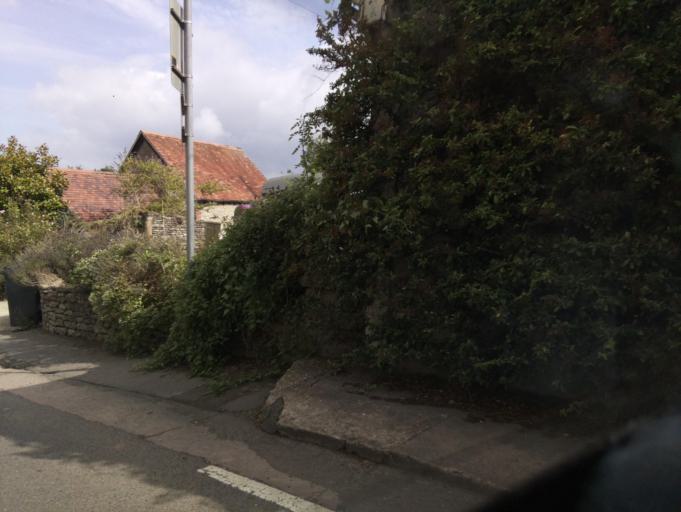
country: GB
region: England
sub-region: Somerset
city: Wincanton
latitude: 51.0012
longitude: -2.4151
